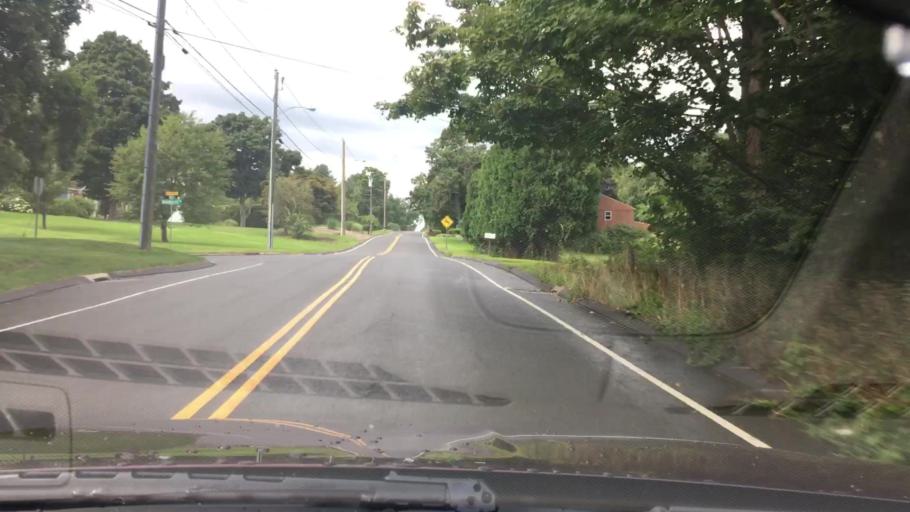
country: US
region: Connecticut
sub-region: Hartford County
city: Manchester
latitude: 41.7378
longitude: -72.5364
